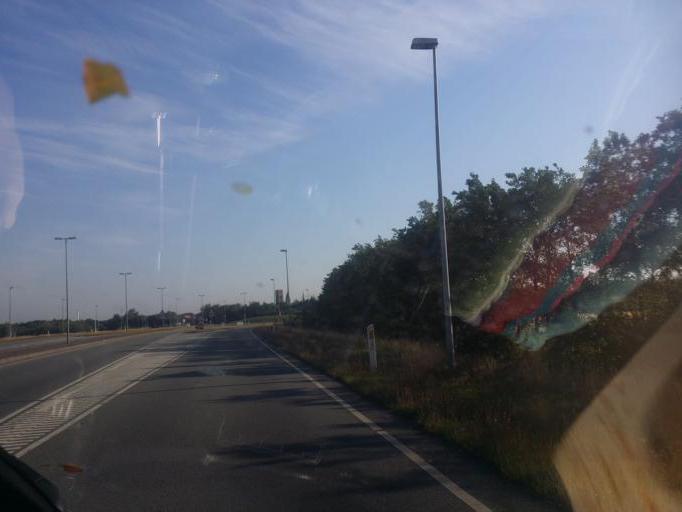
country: DK
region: South Denmark
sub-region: Esbjerg Kommune
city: Ribe
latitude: 55.3194
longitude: 8.7538
